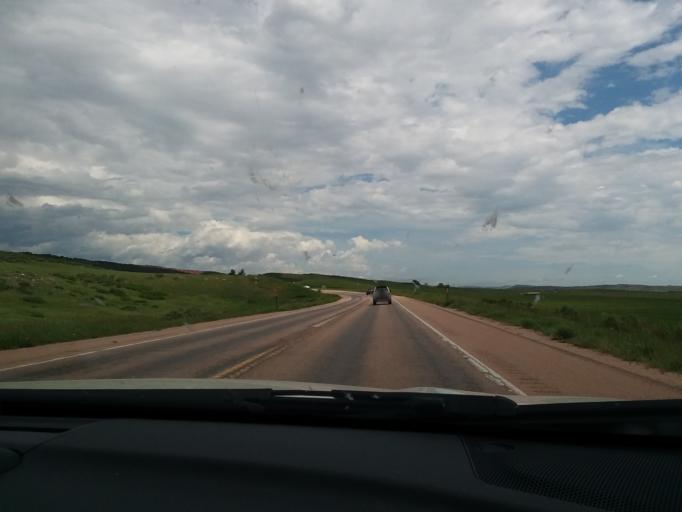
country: US
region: Colorado
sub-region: Larimer County
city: Laporte
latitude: 40.7547
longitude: -105.1710
